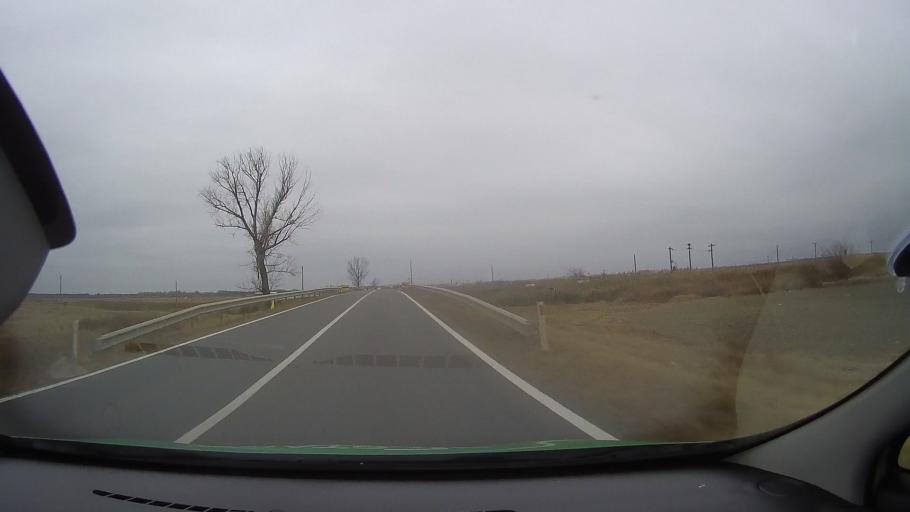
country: RO
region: Ialomita
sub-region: Comuna Slobozia
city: Slobozia
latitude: 44.5911
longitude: 27.3905
